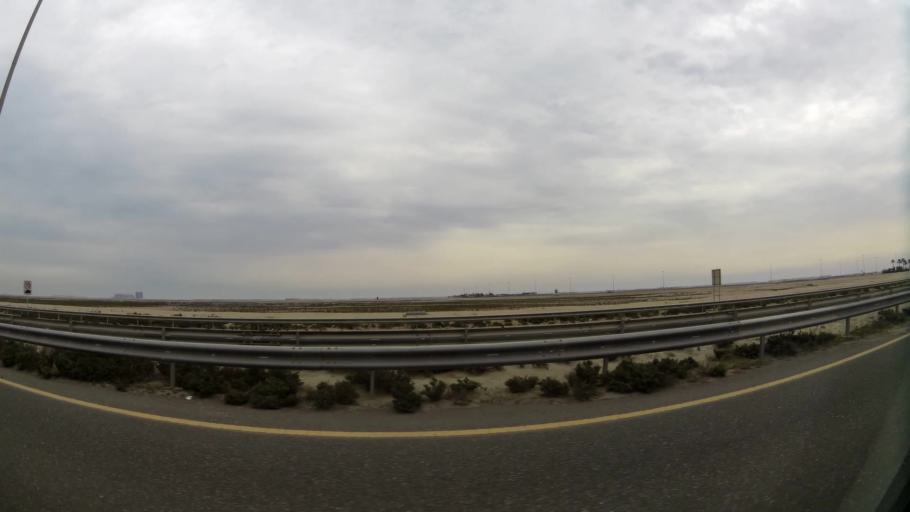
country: BH
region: Central Governorate
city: Dar Kulayb
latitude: 25.8487
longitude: 50.5835
